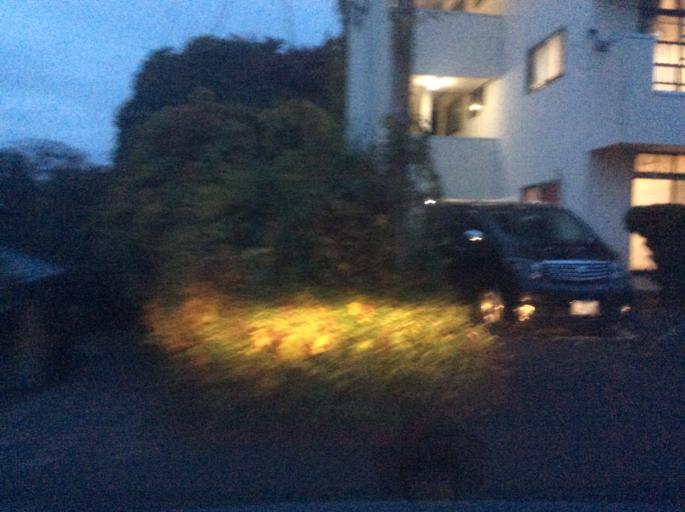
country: JP
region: Fukushima
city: Iwaki
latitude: 37.0627
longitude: 140.8854
